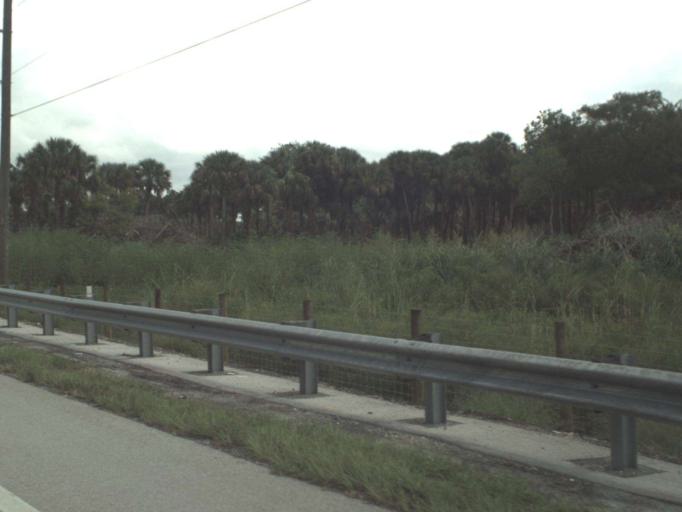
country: US
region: Florida
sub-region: Okeechobee County
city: Taylor Creek
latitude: 27.0956
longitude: -80.6573
